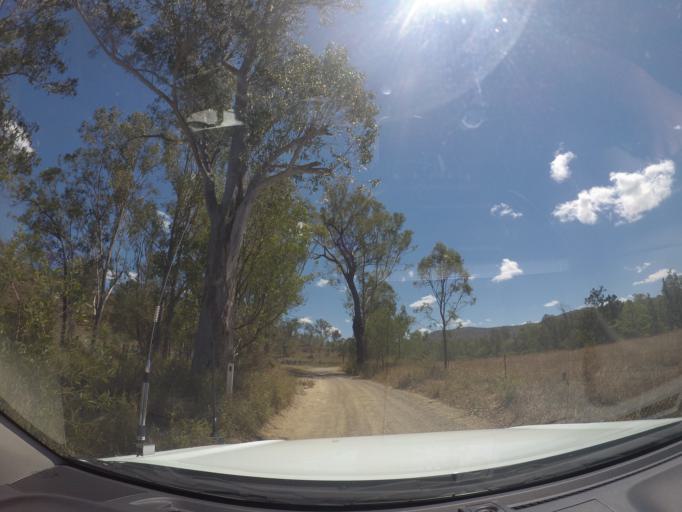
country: AU
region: Queensland
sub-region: Logan
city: North Maclean
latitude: -27.8216
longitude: 152.8579
